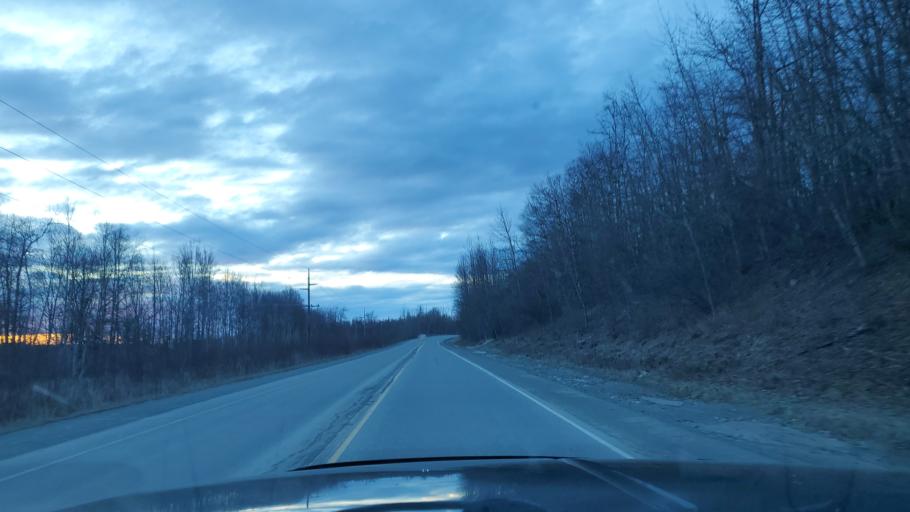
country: US
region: Alaska
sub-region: Matanuska-Susitna Borough
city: Lakes
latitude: 61.6070
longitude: -149.3390
